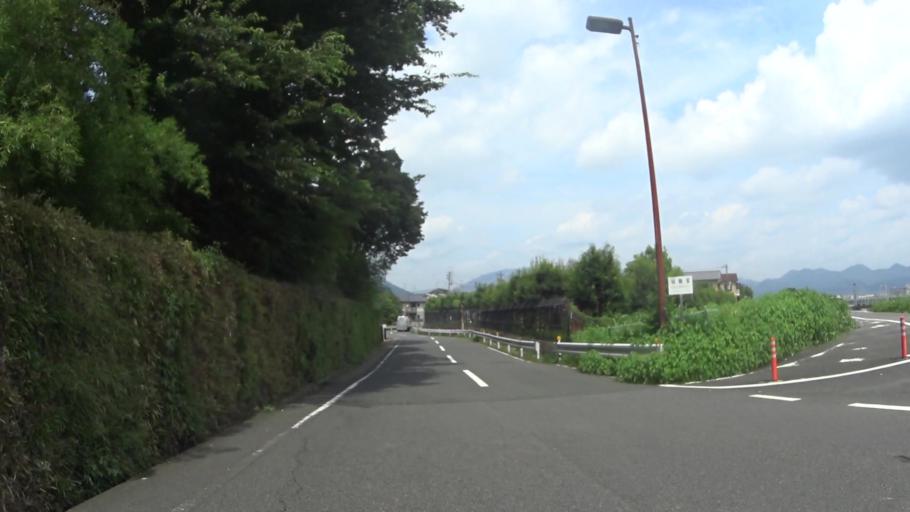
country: JP
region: Kyoto
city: Muko
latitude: 34.9849
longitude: 135.7107
